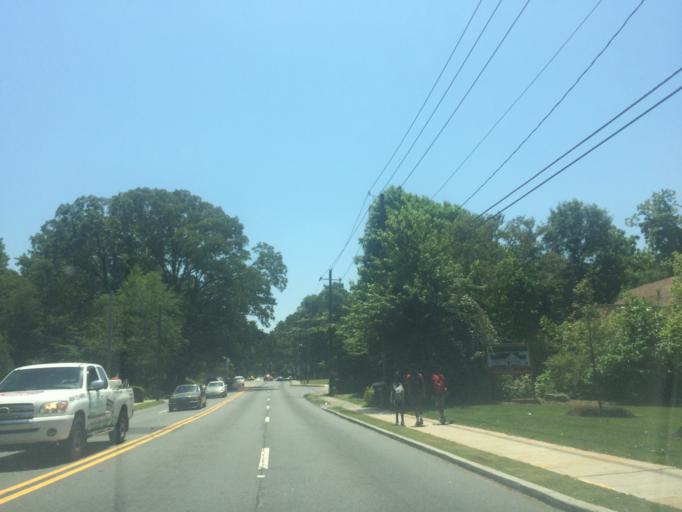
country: US
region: Georgia
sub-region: DeKalb County
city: North Decatur
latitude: 33.7862
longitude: -84.3057
